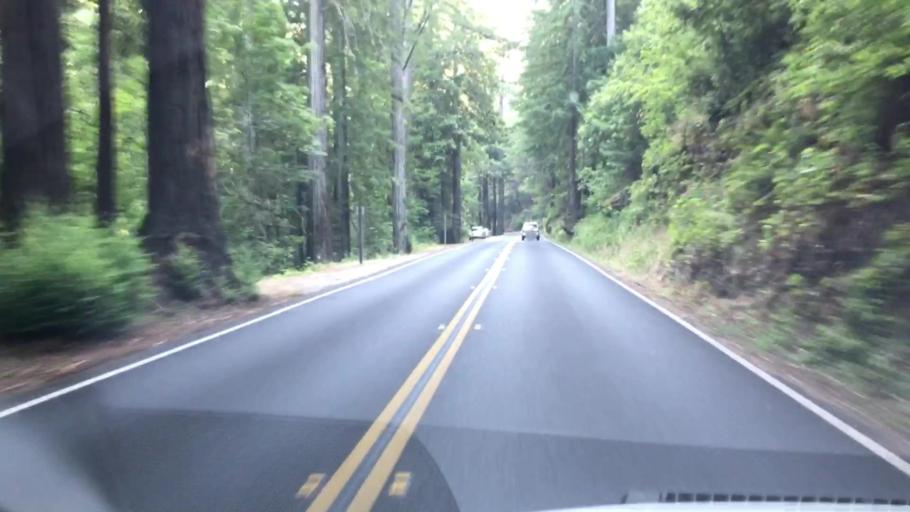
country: US
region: California
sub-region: Marin County
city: Lagunitas-Forest Knolls
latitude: 38.0075
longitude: -122.7115
